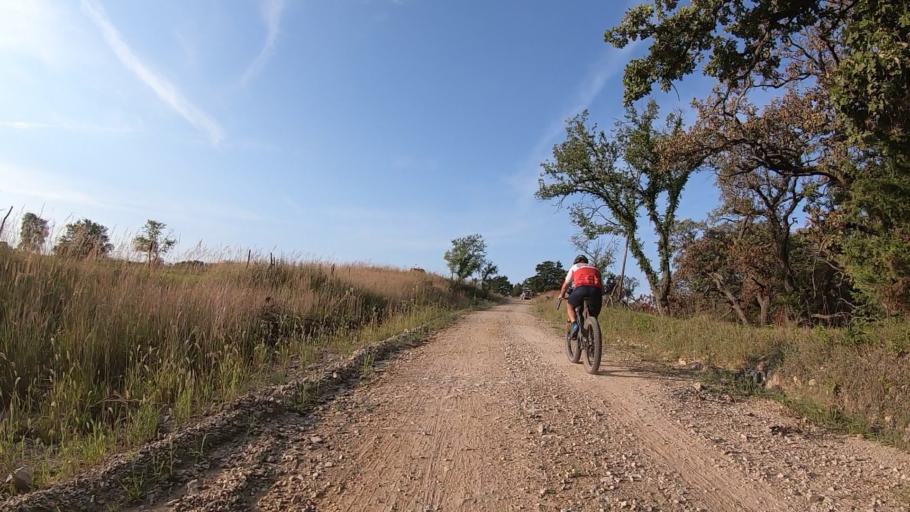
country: US
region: Kansas
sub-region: Marshall County
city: Blue Rapids
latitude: 39.7194
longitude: -96.8064
